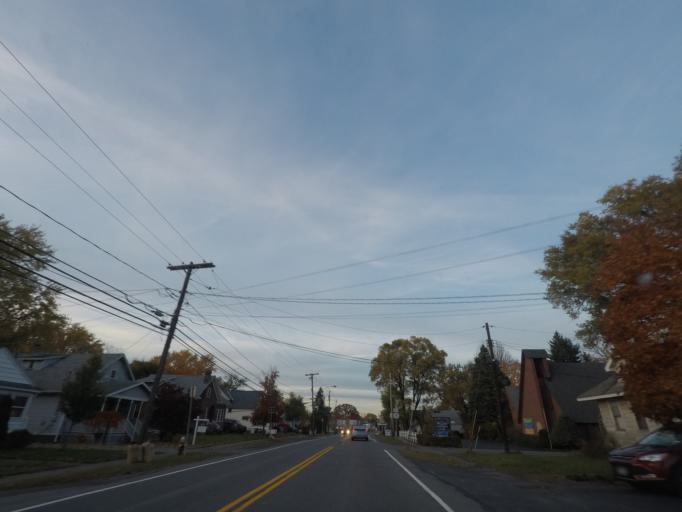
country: US
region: New York
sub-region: Schenectady County
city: Rotterdam
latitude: 42.7848
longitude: -73.9710
